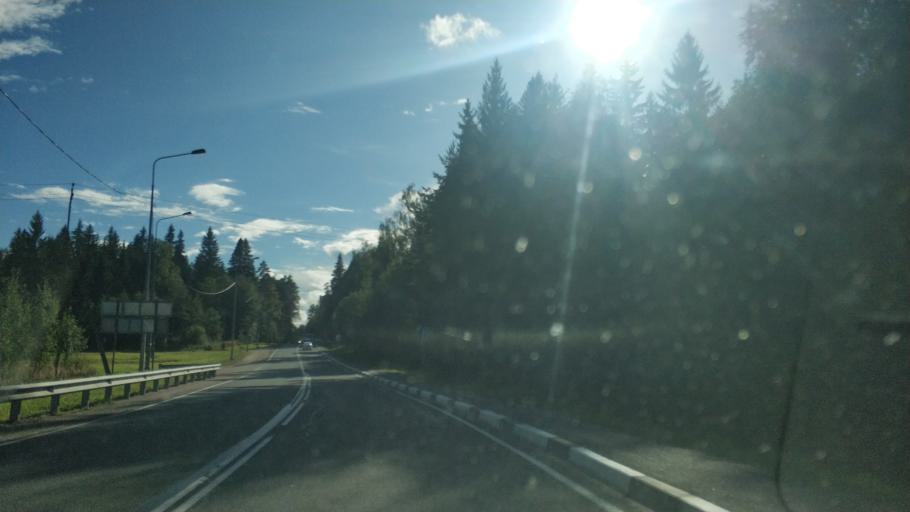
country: RU
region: Republic of Karelia
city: Lakhdenpokh'ya
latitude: 61.5349
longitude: 30.2131
